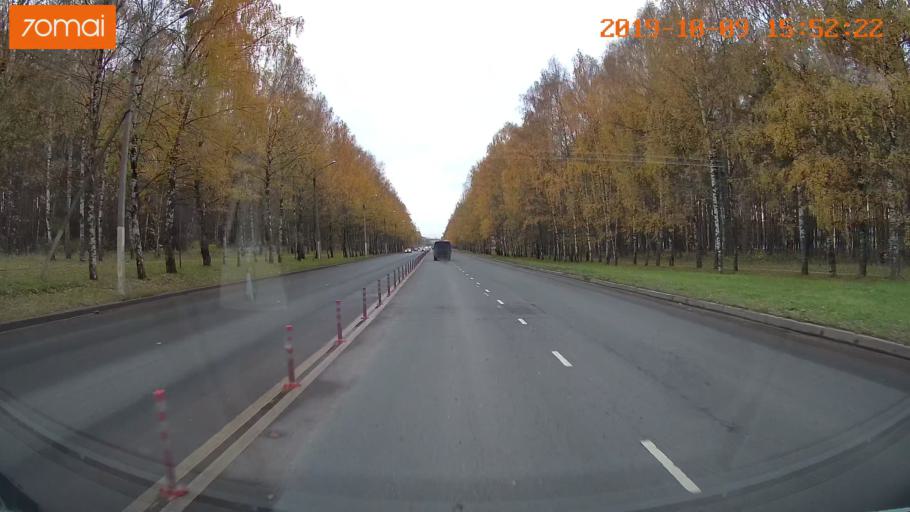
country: RU
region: Kostroma
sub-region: Kostromskoy Rayon
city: Kostroma
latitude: 57.7903
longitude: 40.9689
